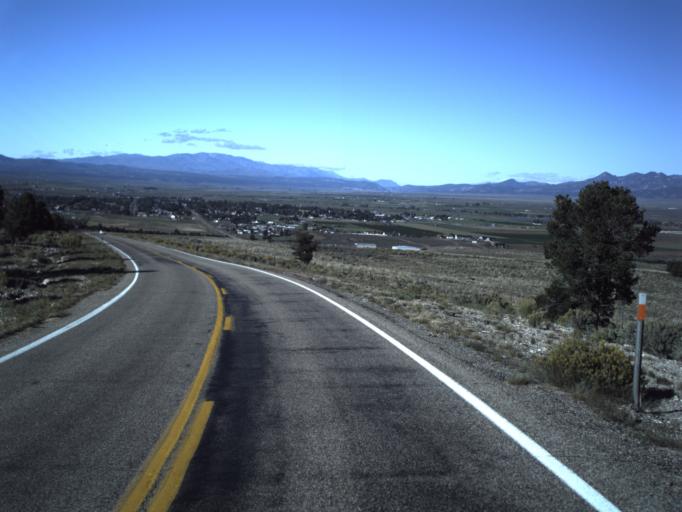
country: US
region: Utah
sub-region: Garfield County
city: Panguitch
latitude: 37.7924
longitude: -112.4369
